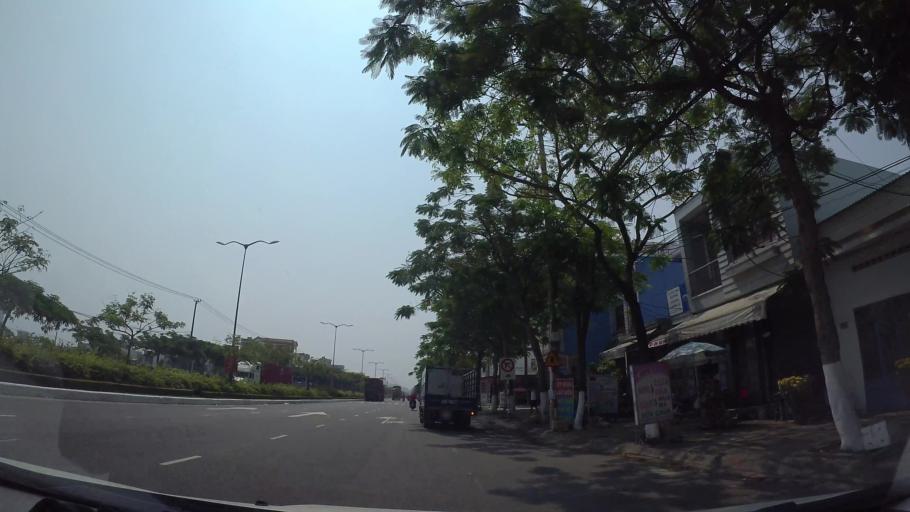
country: VN
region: Da Nang
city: Ngu Hanh Son
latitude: 16.0250
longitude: 108.2497
